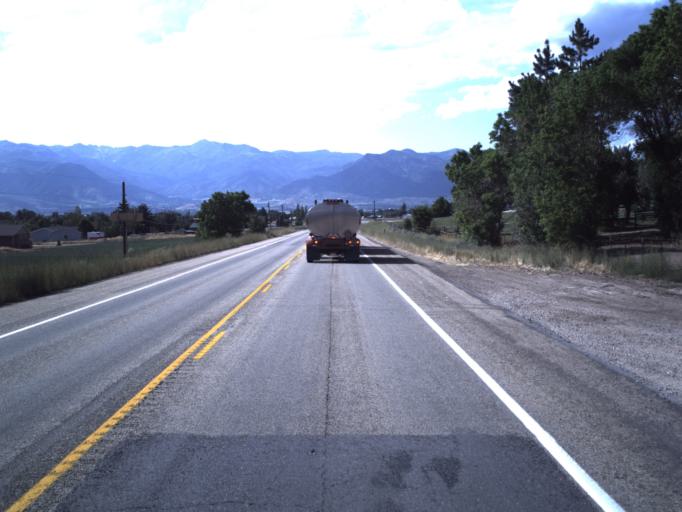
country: US
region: Utah
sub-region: Wasatch County
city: Heber
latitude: 40.4515
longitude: -111.3710
